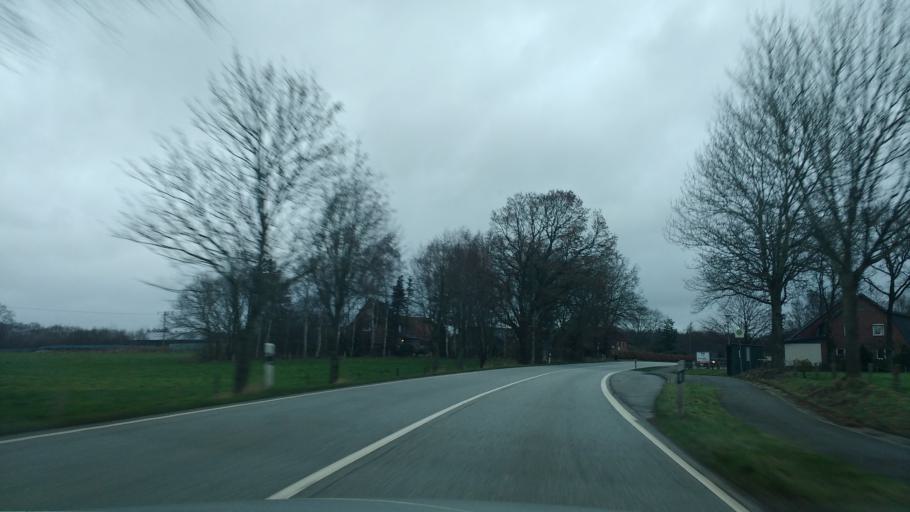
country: DE
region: Schleswig-Holstein
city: Schlotfeld
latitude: 53.9718
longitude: 9.5718
